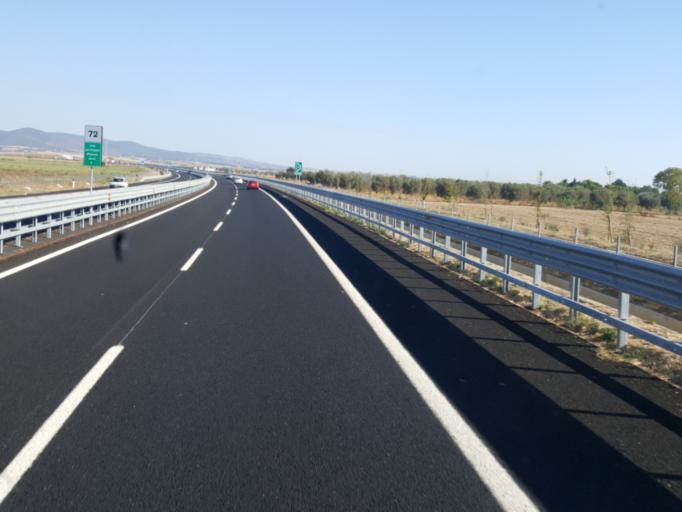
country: IT
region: Latium
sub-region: Provincia di Viterbo
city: Tarquinia
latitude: 42.2203
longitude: 11.7714
